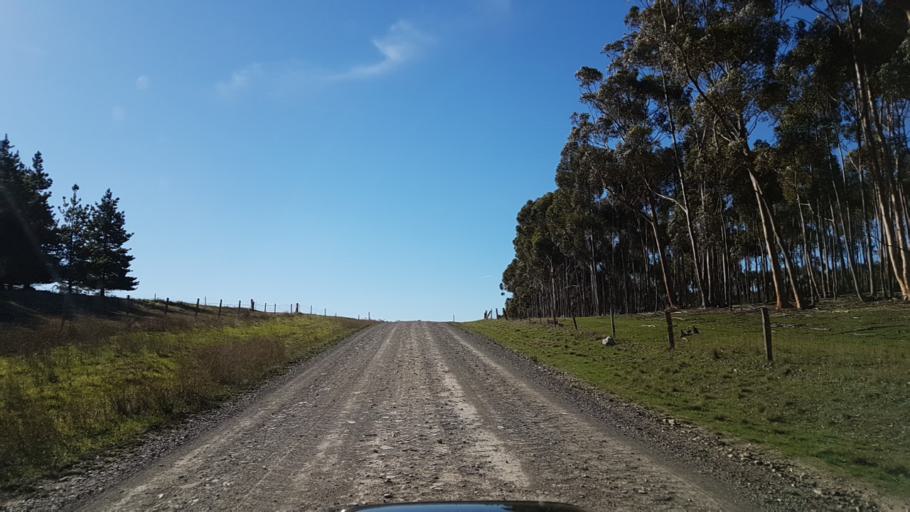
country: AU
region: South Australia
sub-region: Northern Areas
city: Jamestown
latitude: -33.2821
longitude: 138.5595
